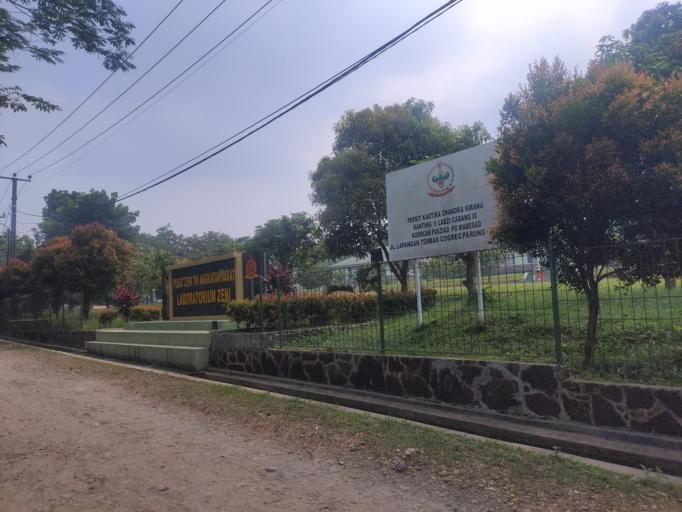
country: ID
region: West Java
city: Parung
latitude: -6.4246
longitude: 106.6994
